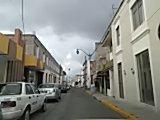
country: MX
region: Nayarit
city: Tepic
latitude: 21.5086
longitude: -104.8958
